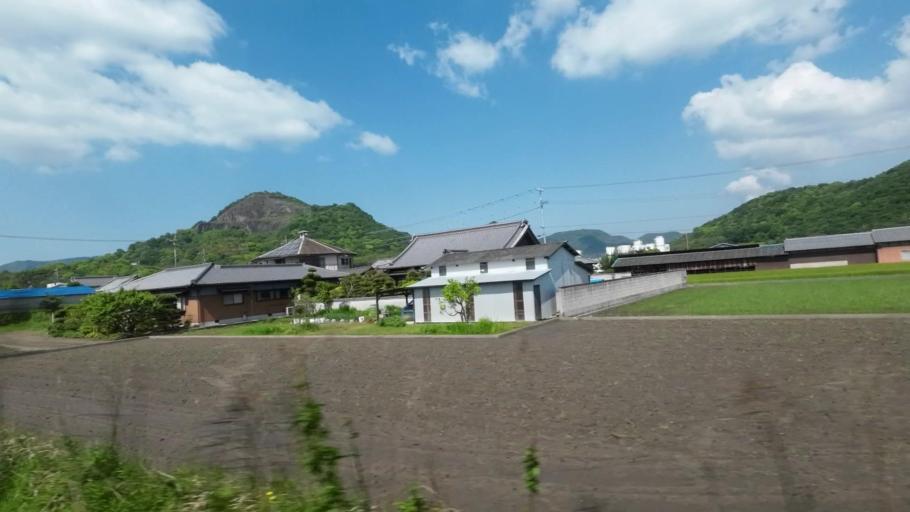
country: JP
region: Kagawa
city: Kan'onjicho
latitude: 34.1901
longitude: 133.7130
